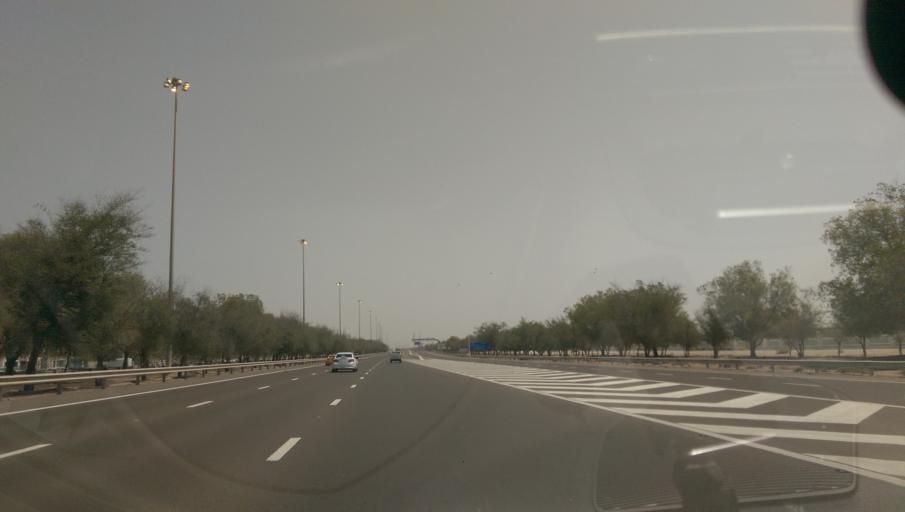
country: AE
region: Abu Dhabi
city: Abu Dhabi
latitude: 24.5302
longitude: 54.6925
